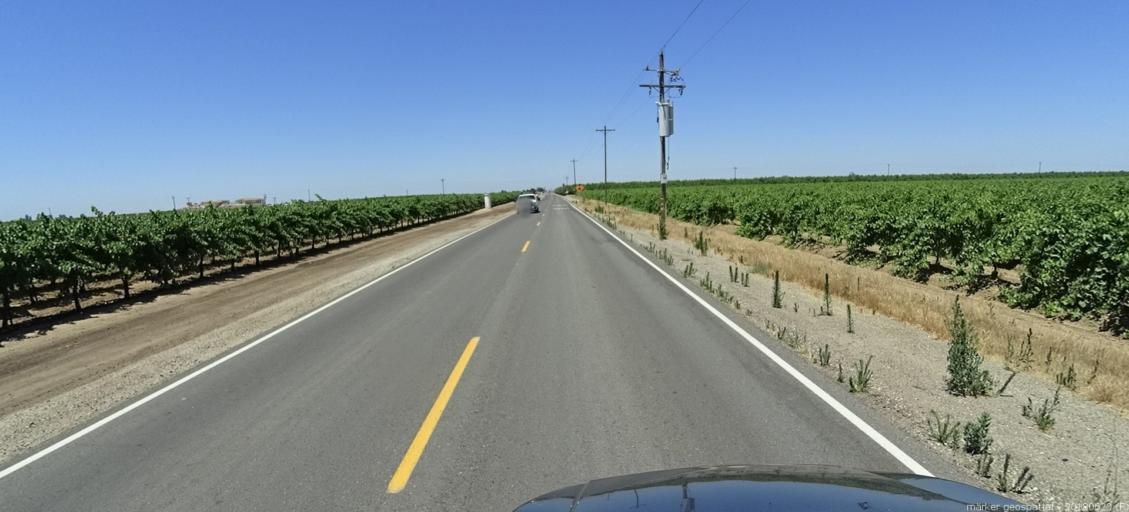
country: US
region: California
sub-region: Madera County
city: Parkwood
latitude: 36.8804
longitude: -119.9983
